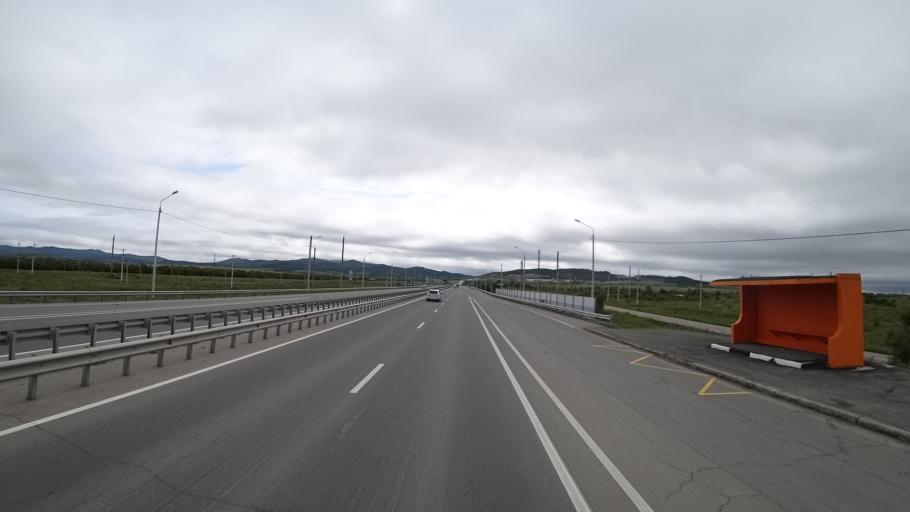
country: RU
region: Primorskiy
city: Monastyrishche
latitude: 44.1879
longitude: 132.4412
